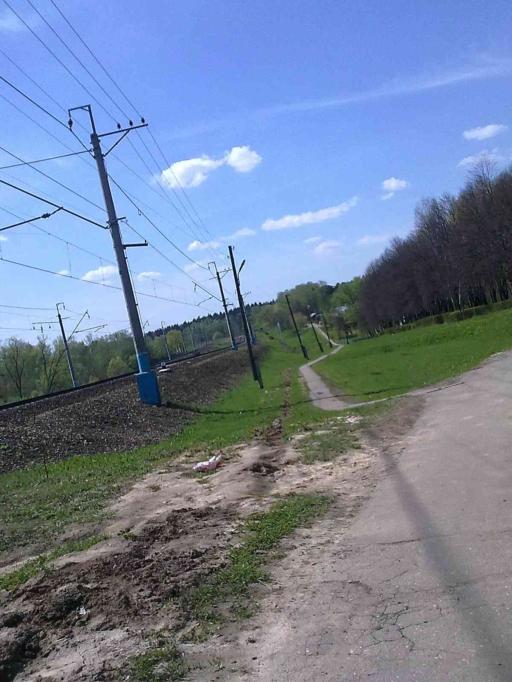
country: RU
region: Moscow
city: Novo-Peredelkino
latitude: 55.6550
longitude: 37.3461
